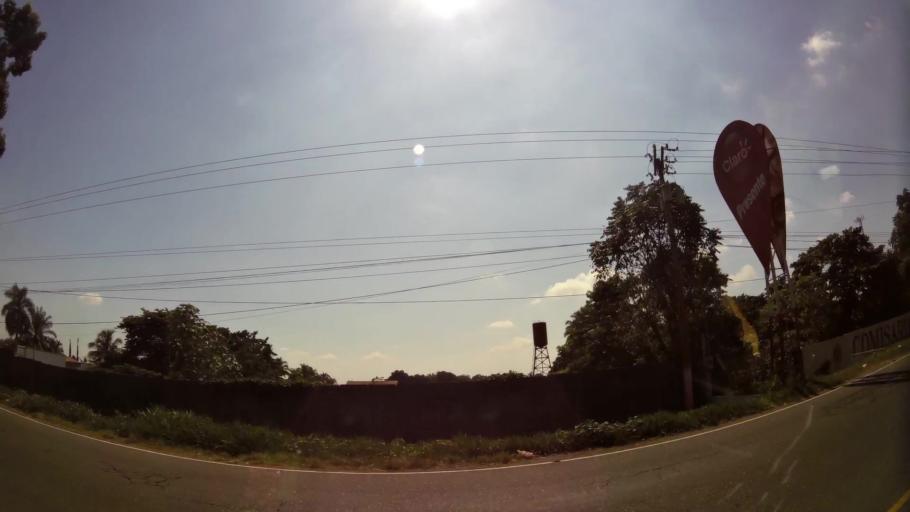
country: GT
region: Suchitepeque
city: Mazatenango
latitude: 14.5334
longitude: -91.4916
